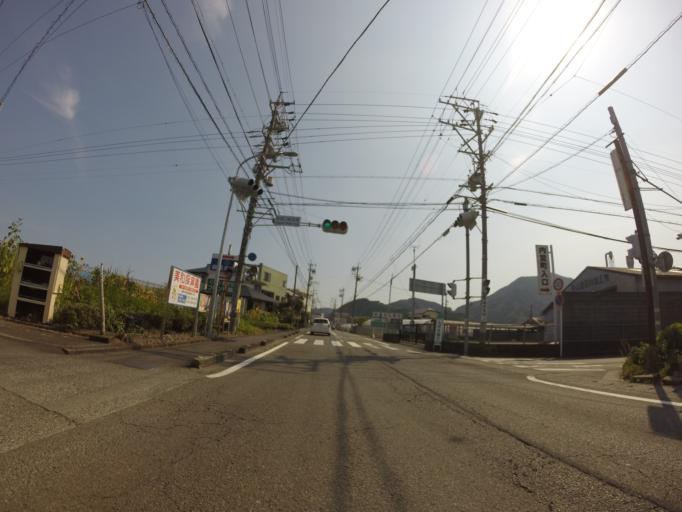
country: JP
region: Shizuoka
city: Shizuoka-shi
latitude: 35.0168
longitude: 138.3589
